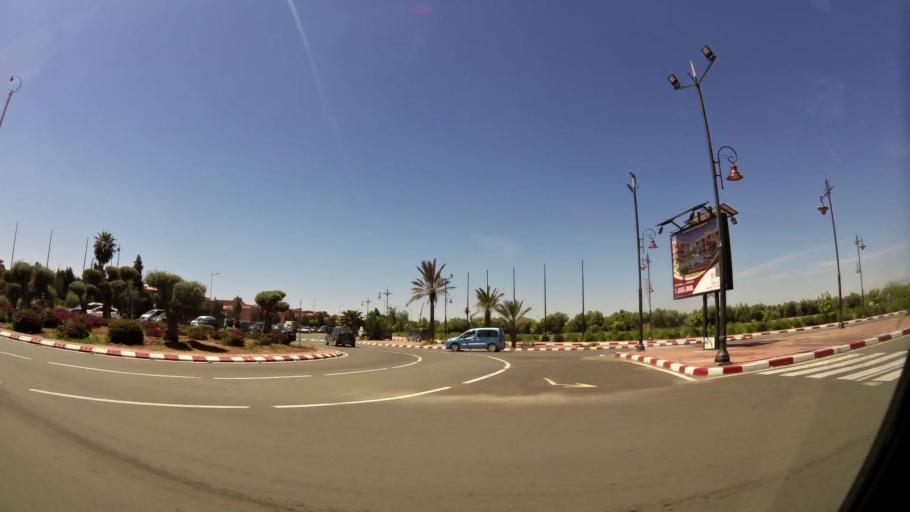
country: MA
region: Marrakech-Tensift-Al Haouz
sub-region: Marrakech
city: Marrakesh
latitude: 31.6153
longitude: -7.9955
